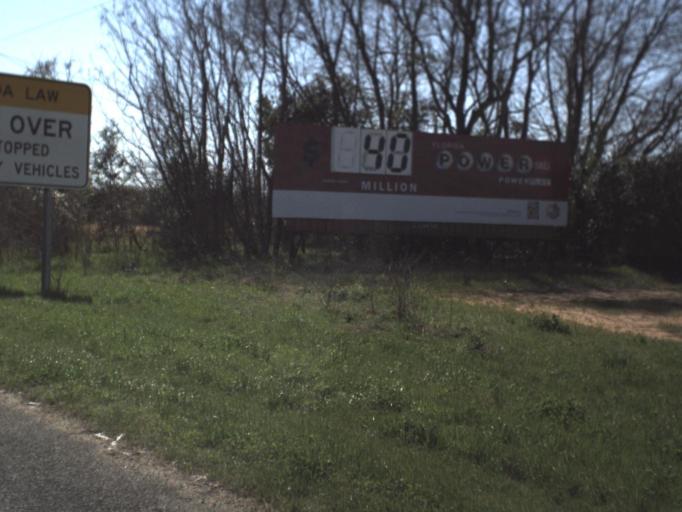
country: US
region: Florida
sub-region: Jackson County
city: Graceville
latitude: 30.9896
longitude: -85.4080
